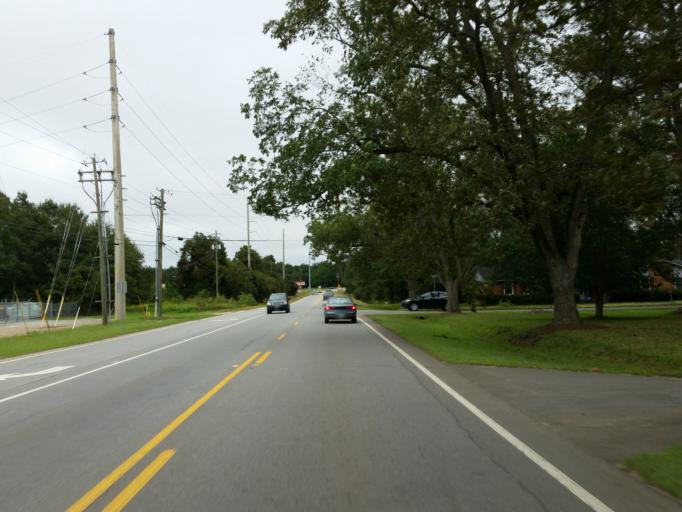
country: US
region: Georgia
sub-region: Peach County
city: Fort Valley
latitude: 32.5745
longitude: -83.8991
